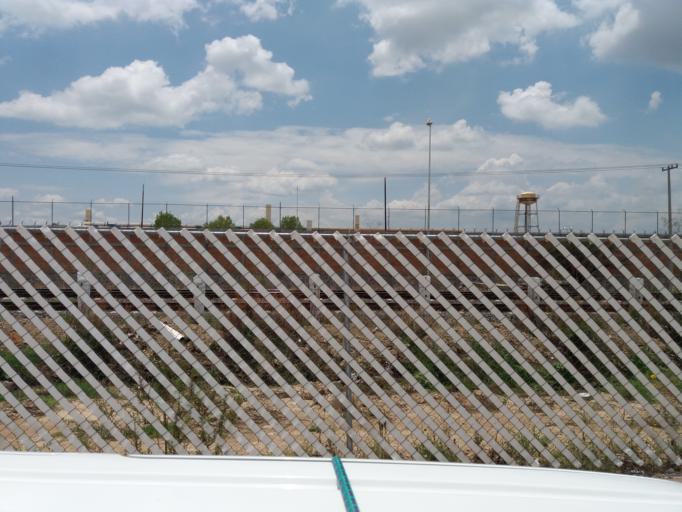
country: MX
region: Aguascalientes
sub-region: Aguascalientes
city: San Sebastian [Fraccionamiento]
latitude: 21.8048
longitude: -102.2764
